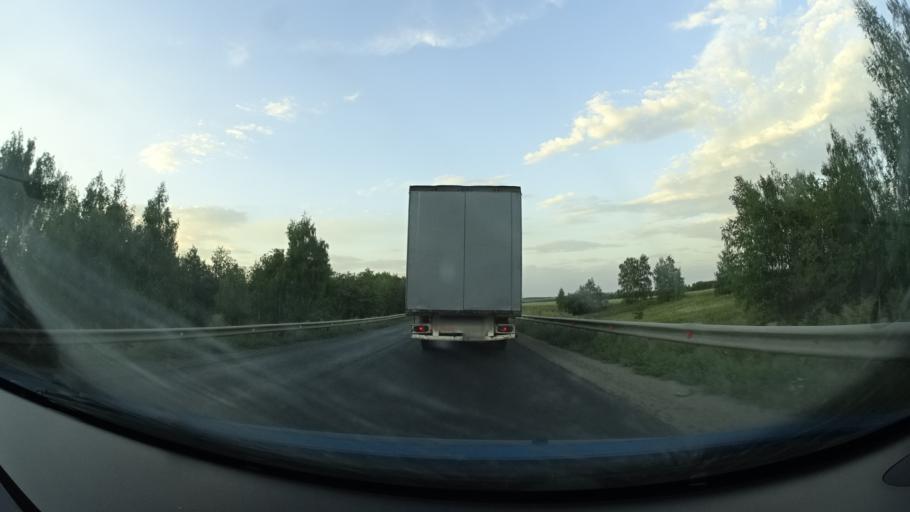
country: RU
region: Orenburg
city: Severnoye
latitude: 54.1521
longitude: 52.6190
